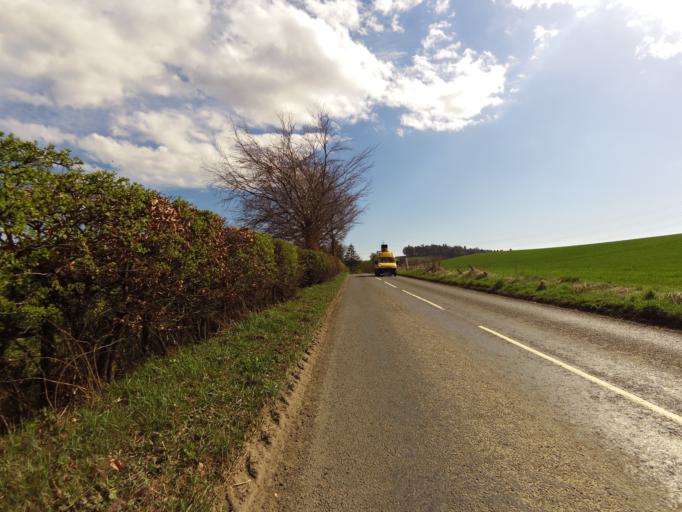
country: GB
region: Scotland
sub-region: Fife
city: Auchtermuchty
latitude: 56.3106
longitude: -3.2354
